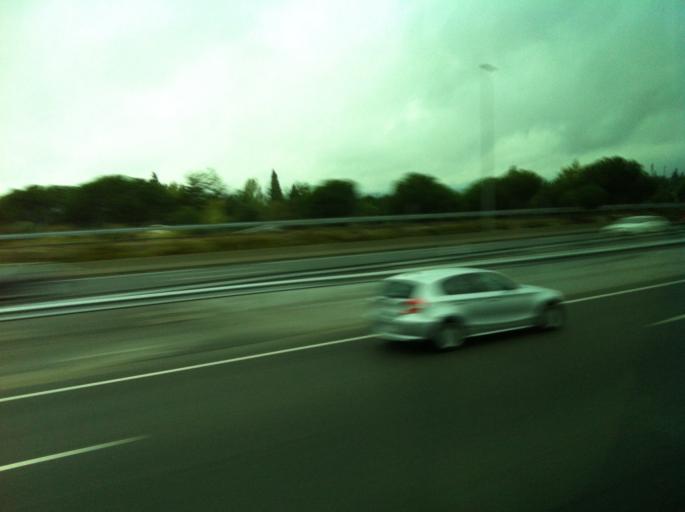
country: ES
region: Madrid
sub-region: Provincia de Madrid
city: Torrelodones
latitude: 40.6018
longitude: -3.9639
